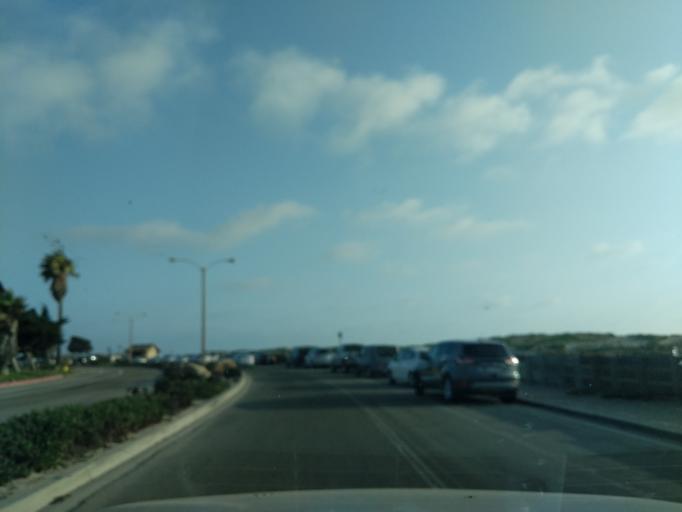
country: US
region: California
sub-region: Ventura County
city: Ventura
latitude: 34.2416
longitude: -119.2660
